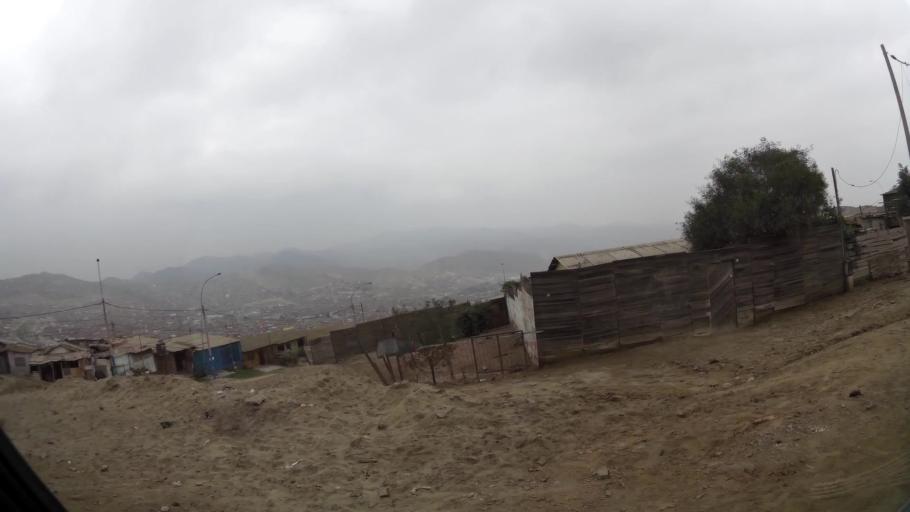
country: PE
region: Lima
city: Ventanilla
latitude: -11.8500
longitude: -77.1324
